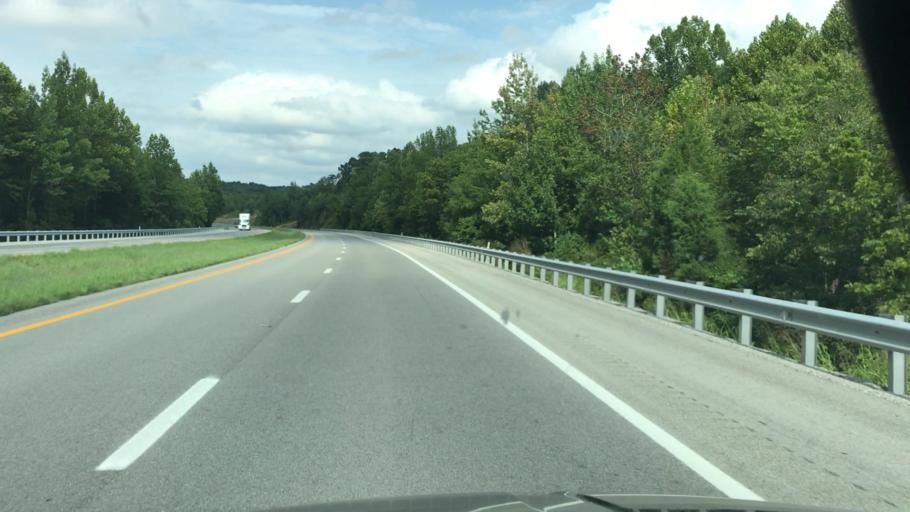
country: US
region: Kentucky
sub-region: Hopkins County
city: Dawson Springs
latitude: 37.1573
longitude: -87.7680
